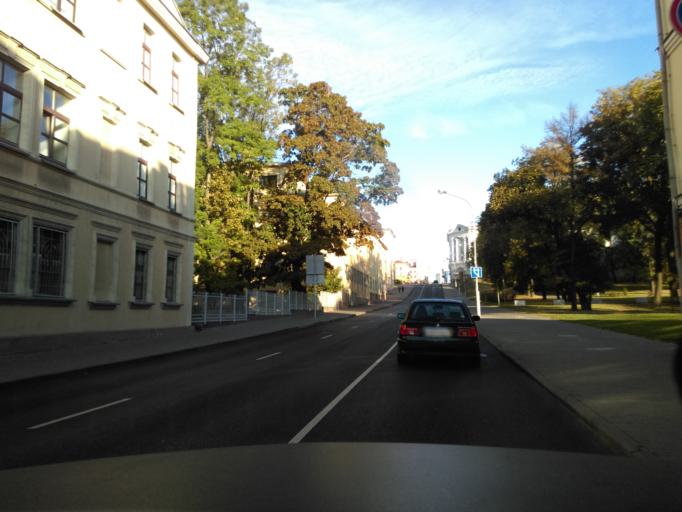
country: BY
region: Minsk
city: Minsk
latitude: 53.8964
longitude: 27.5644
